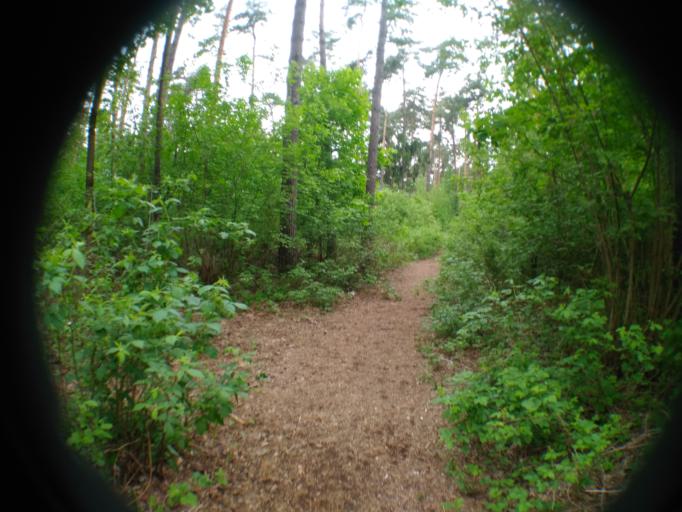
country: RU
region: Moskovskaya
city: Zhukovskiy
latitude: 55.5818
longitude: 38.1323
